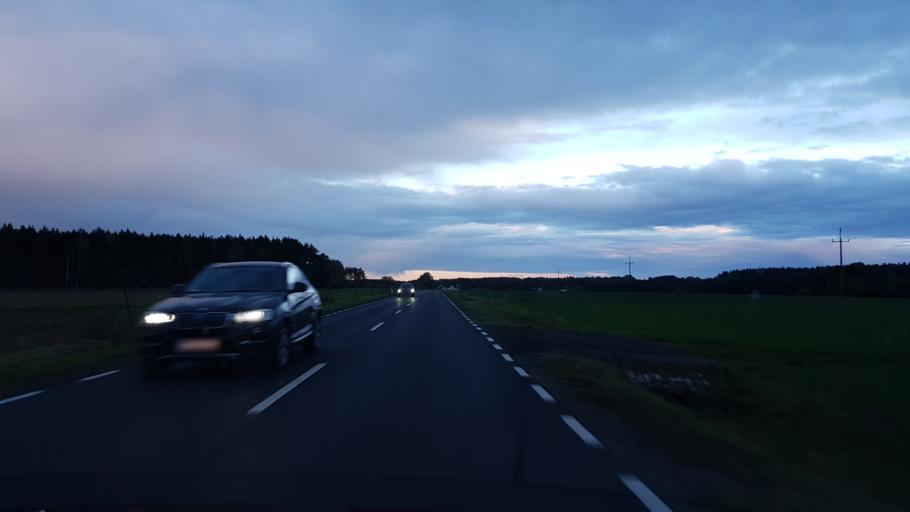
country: PL
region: Greater Poland Voivodeship
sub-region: Powiat zlotowski
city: Krajenka
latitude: 53.2708
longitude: 16.9358
